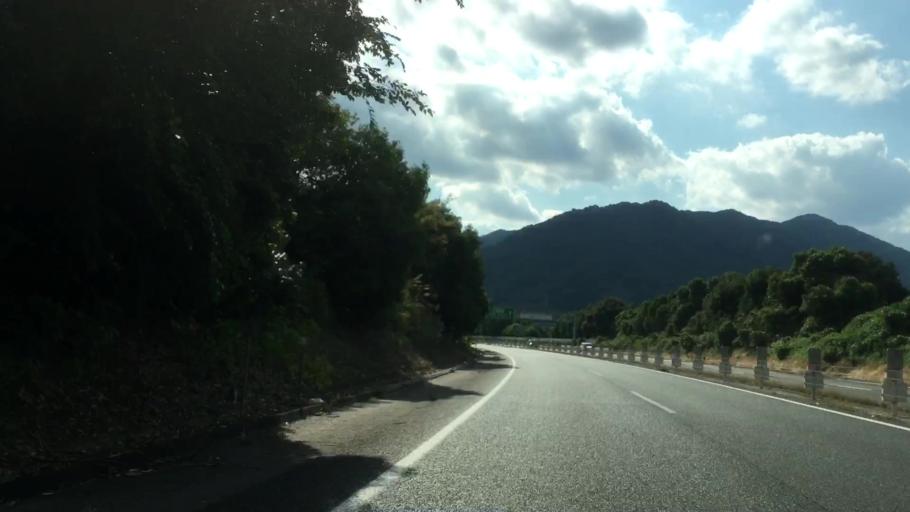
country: JP
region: Hiroshima
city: Hatsukaichi
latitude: 34.3444
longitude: 132.3071
